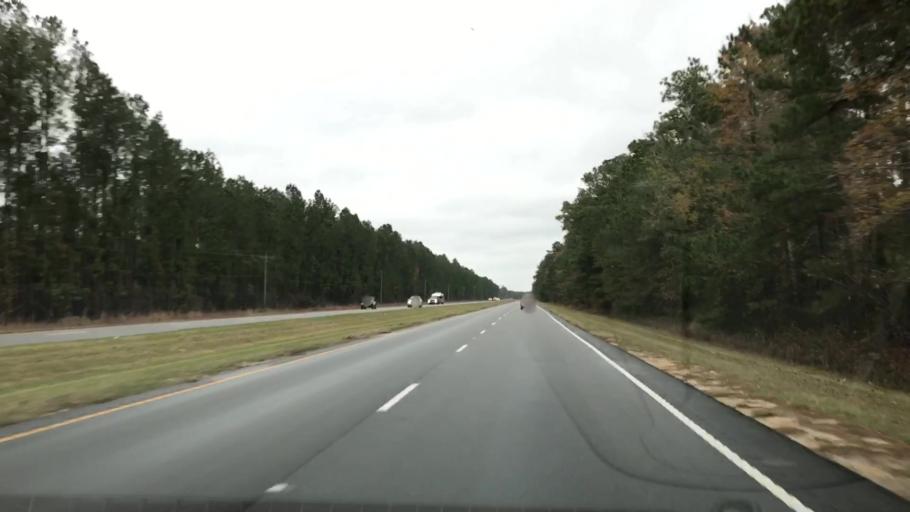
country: US
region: South Carolina
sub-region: Georgetown County
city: Georgetown
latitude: 33.2786
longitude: -79.3511
